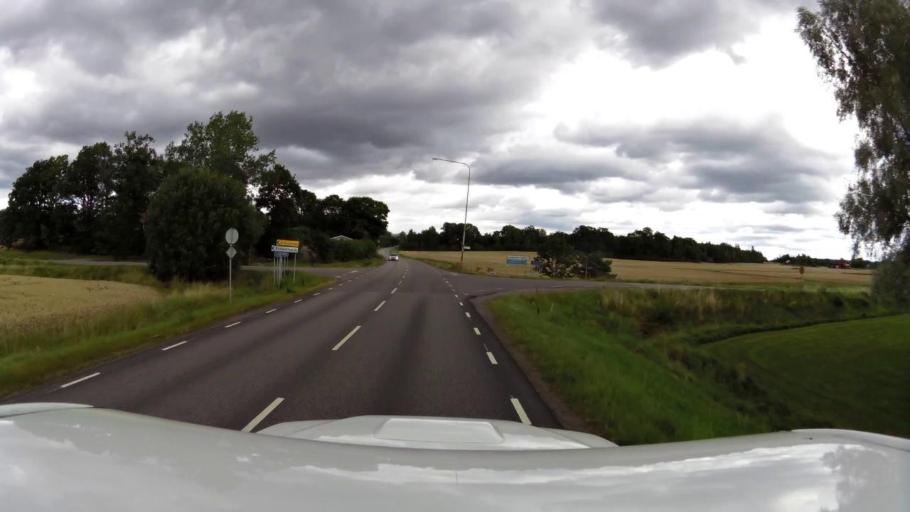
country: SE
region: OEstergoetland
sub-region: Linkopings Kommun
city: Sturefors
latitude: 58.3776
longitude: 15.7206
